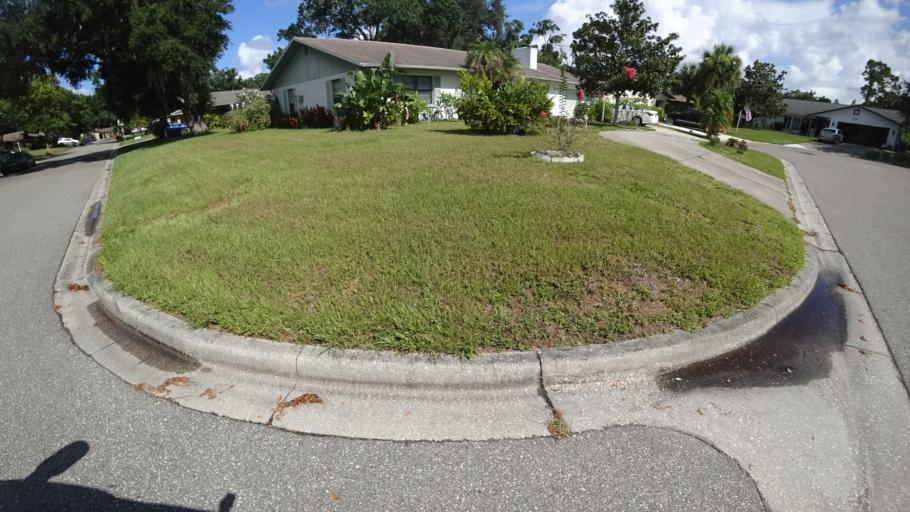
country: US
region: Florida
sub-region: Sarasota County
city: Desoto Lakes
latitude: 27.3913
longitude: -82.4967
